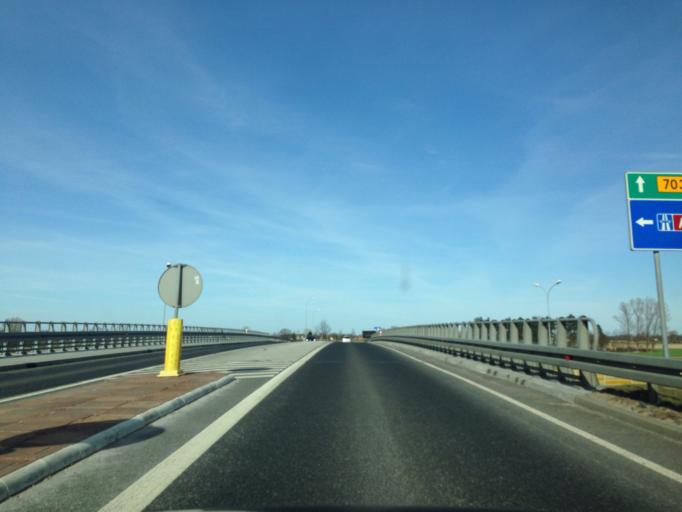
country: PL
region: Lodz Voivodeship
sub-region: Powiat poddebicki
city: Wartkowice
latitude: 51.9929
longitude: 19.0442
